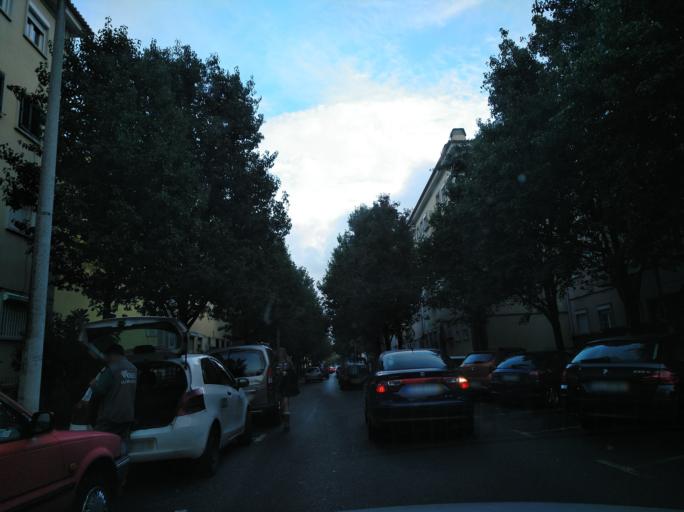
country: PT
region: Lisbon
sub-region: Lisbon
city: Lisbon
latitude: 38.7533
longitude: -9.1490
